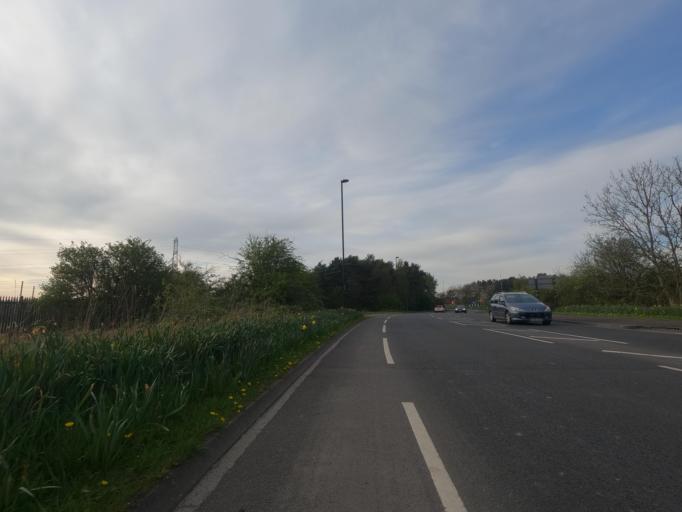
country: GB
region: England
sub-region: Newcastle upon Tyne
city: Hazlerigg
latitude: 55.0634
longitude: -1.6323
